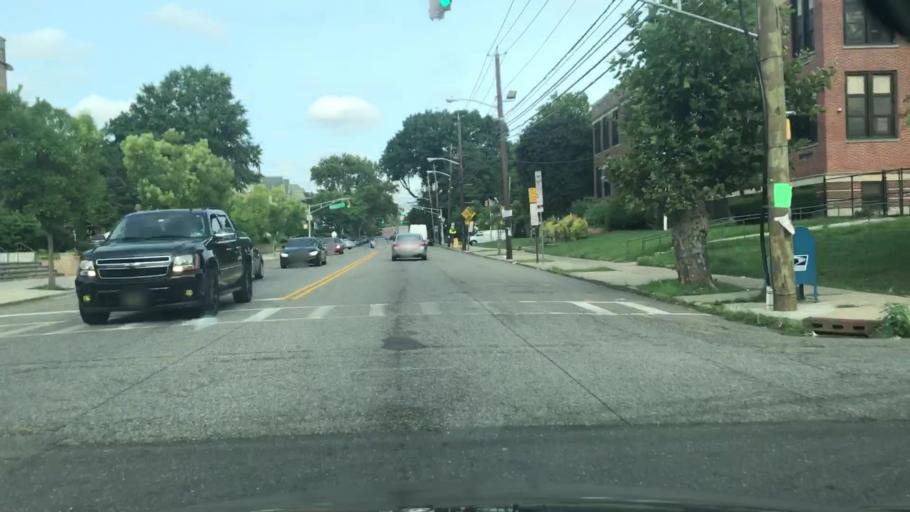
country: US
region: New Jersey
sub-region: Union County
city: Elizabeth
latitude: 40.6794
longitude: -74.2019
